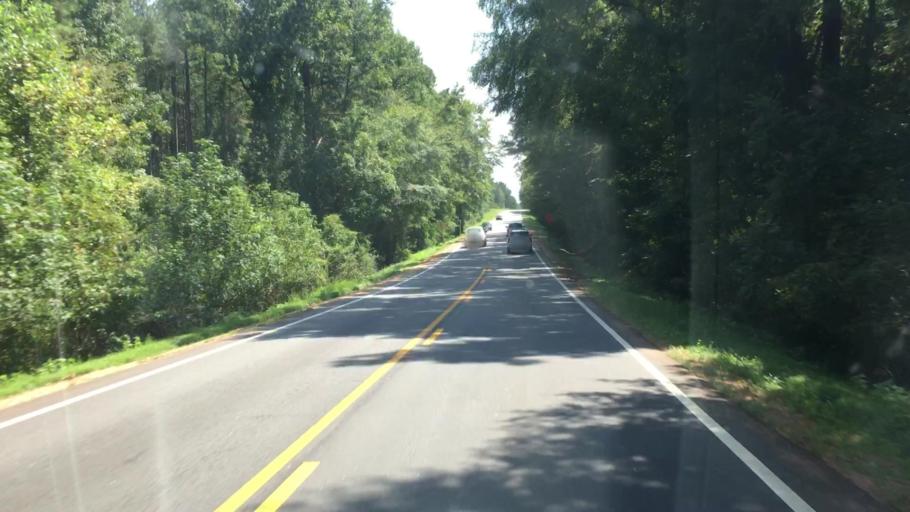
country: US
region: Georgia
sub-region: Oconee County
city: Watkinsville
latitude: 33.7891
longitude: -83.4241
